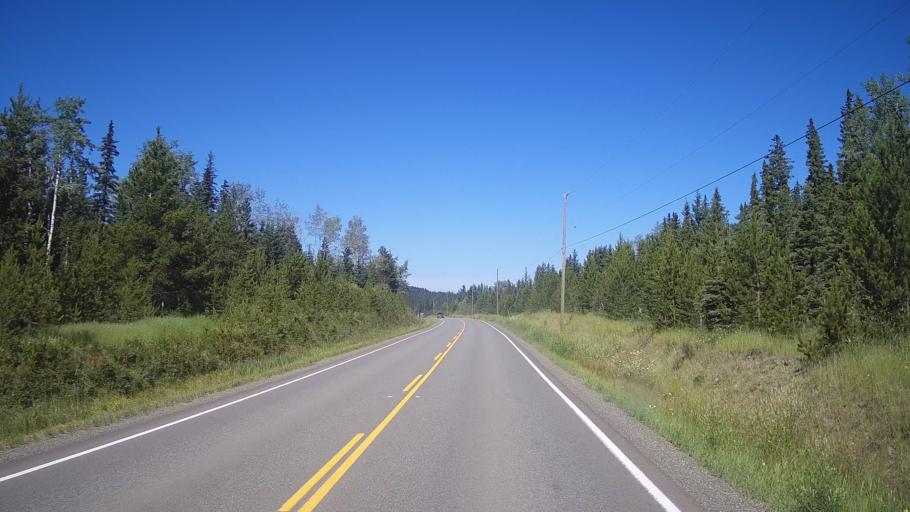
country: CA
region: British Columbia
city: Cache Creek
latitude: 51.5454
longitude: -121.0689
